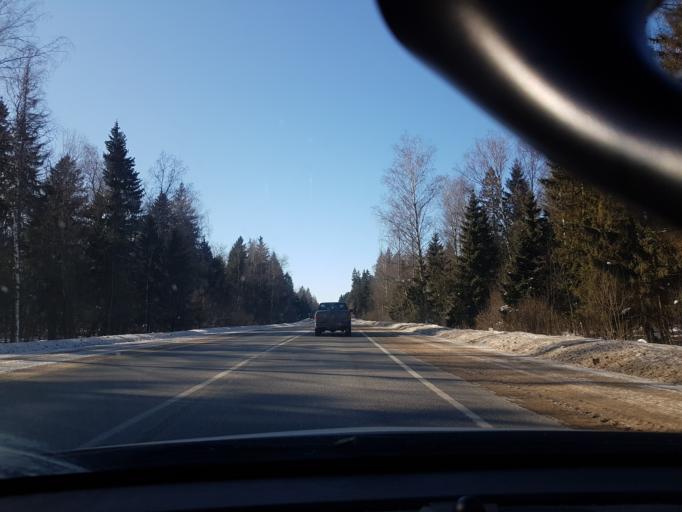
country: RU
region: Moskovskaya
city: Kostrovo
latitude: 55.9130
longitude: 36.7089
